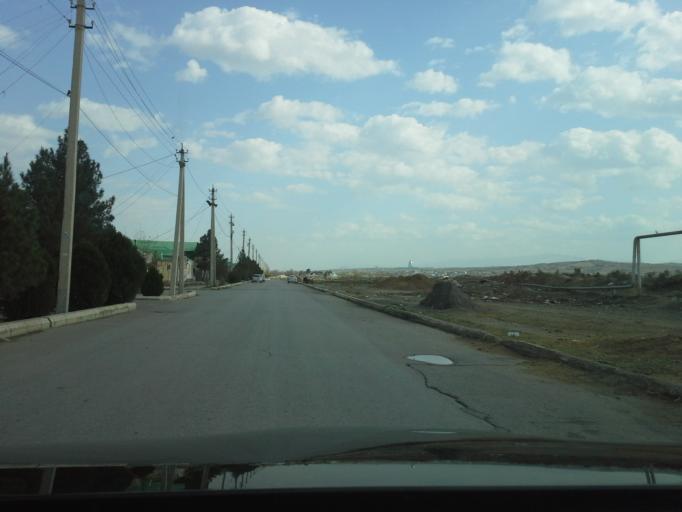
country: TM
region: Ahal
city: Ashgabat
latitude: 37.9846
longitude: 58.2843
